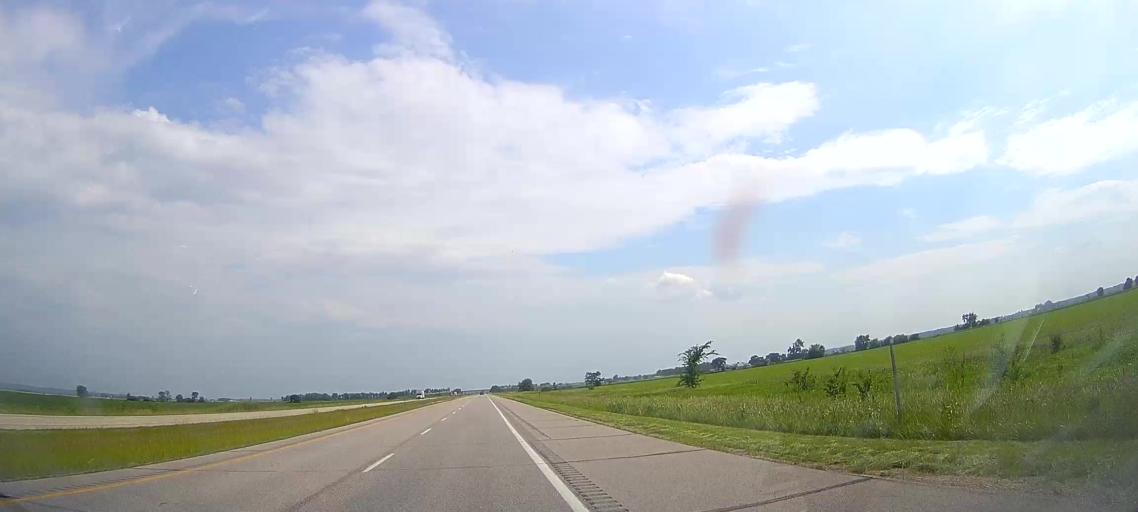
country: US
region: Iowa
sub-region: Monona County
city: Onawa
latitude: 41.8986
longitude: -96.1044
